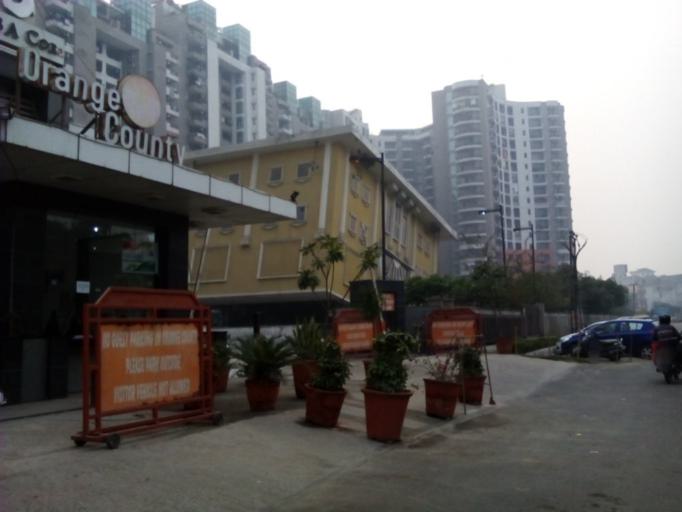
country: IN
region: Uttar Pradesh
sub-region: Gautam Buddha Nagar
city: Noida
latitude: 28.6412
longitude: 77.3622
